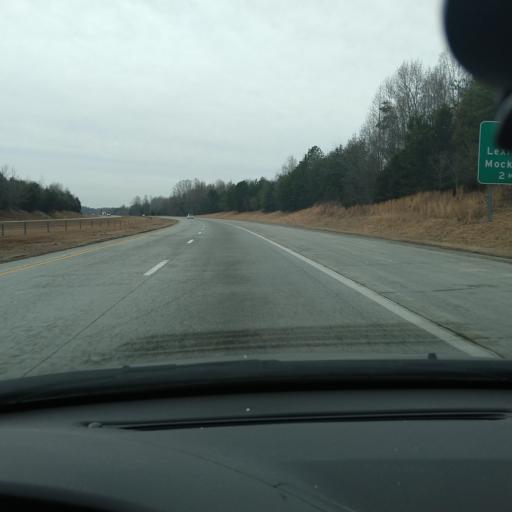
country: US
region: North Carolina
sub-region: Davidson County
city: Welcome
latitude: 35.8673
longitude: -80.2667
